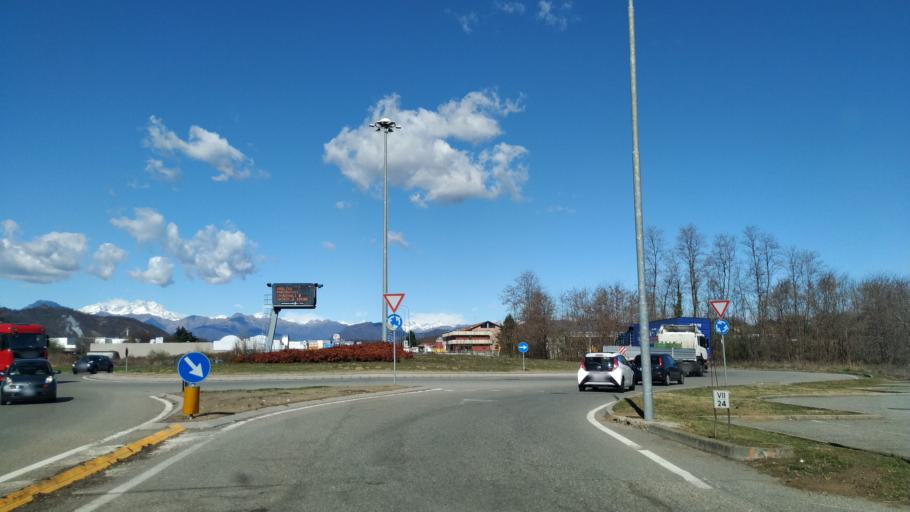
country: IT
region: Piedmont
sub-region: Provincia di Novara
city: Ghemme
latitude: 45.6123
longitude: 8.4085
